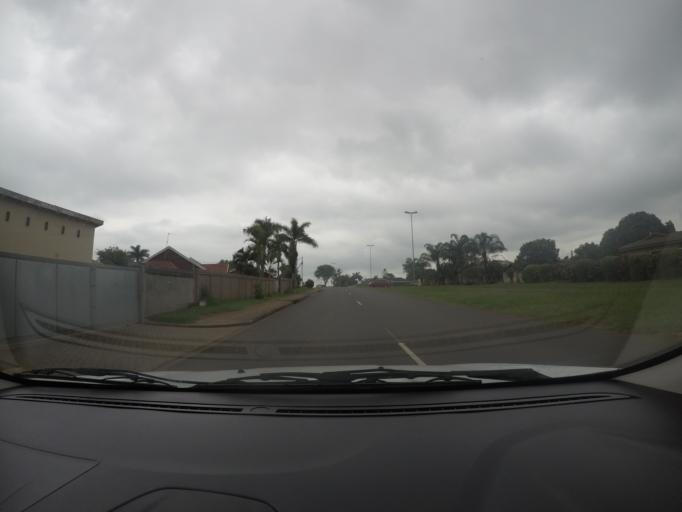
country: ZA
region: KwaZulu-Natal
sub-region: uThungulu District Municipality
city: Empangeni
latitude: -28.7636
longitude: 31.8961
